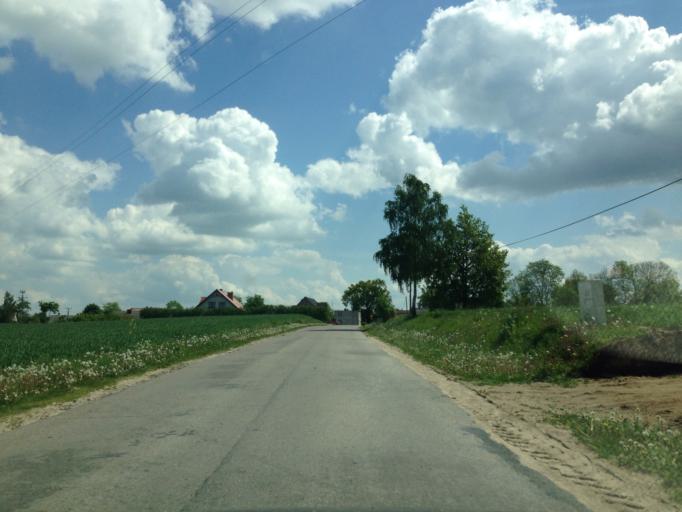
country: PL
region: Kujawsko-Pomorskie
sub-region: Powiat brodnicki
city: Brodnica
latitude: 53.3340
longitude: 19.3714
